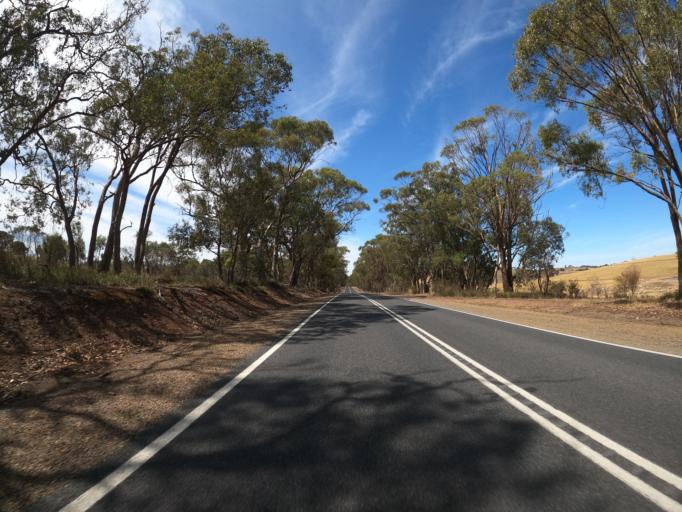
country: AU
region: Victoria
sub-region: Benalla
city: Benalla
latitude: -36.3757
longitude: 145.9747
